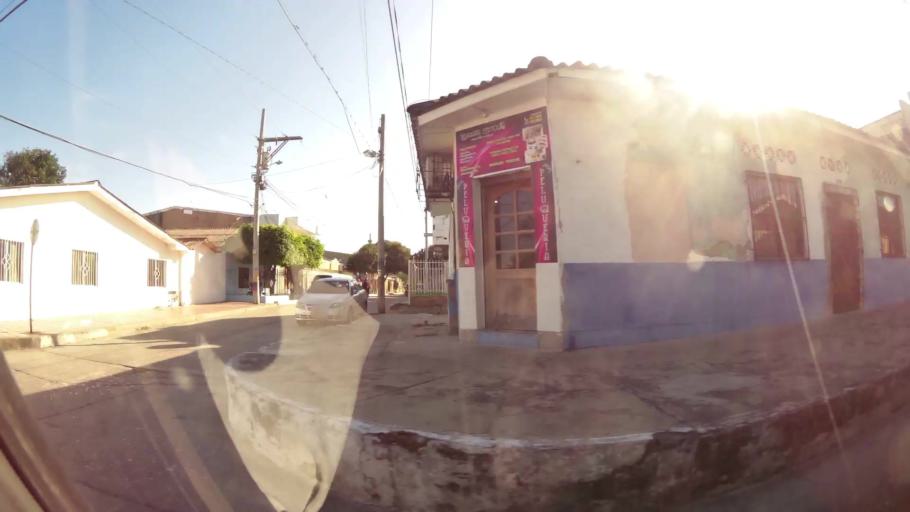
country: CO
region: Atlantico
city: Barranquilla
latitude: 10.9620
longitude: -74.7867
